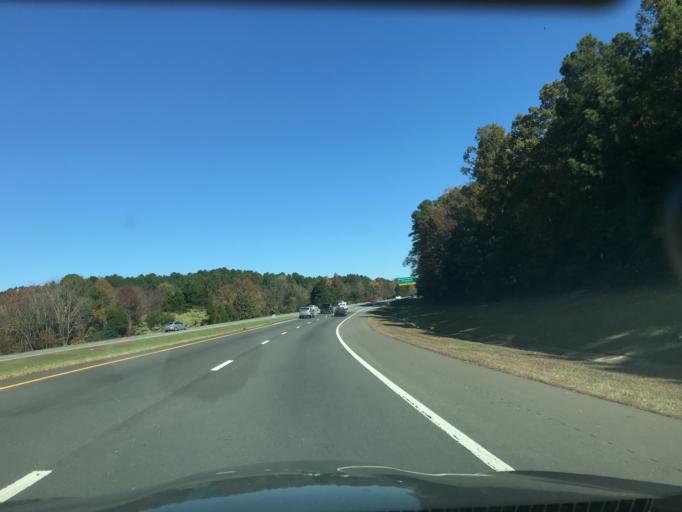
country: US
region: North Carolina
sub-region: Wake County
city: Morrisville
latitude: 35.9043
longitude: -78.8706
